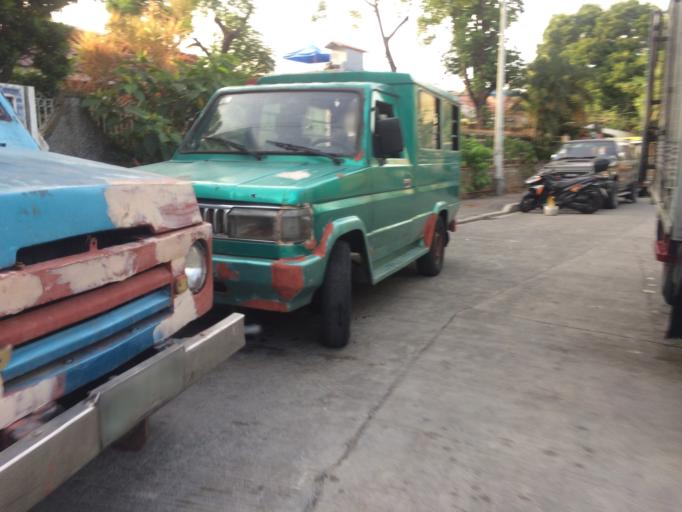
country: PH
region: Calabarzon
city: Bagong Pagasa
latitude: 14.6770
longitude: 121.0220
